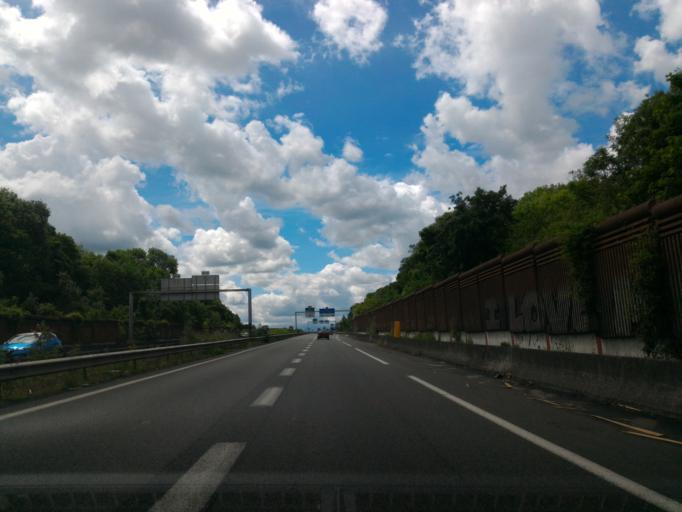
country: FR
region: Ile-de-France
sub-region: Departement de Seine-et-Marne
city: Lognes
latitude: 48.8358
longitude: 2.6231
